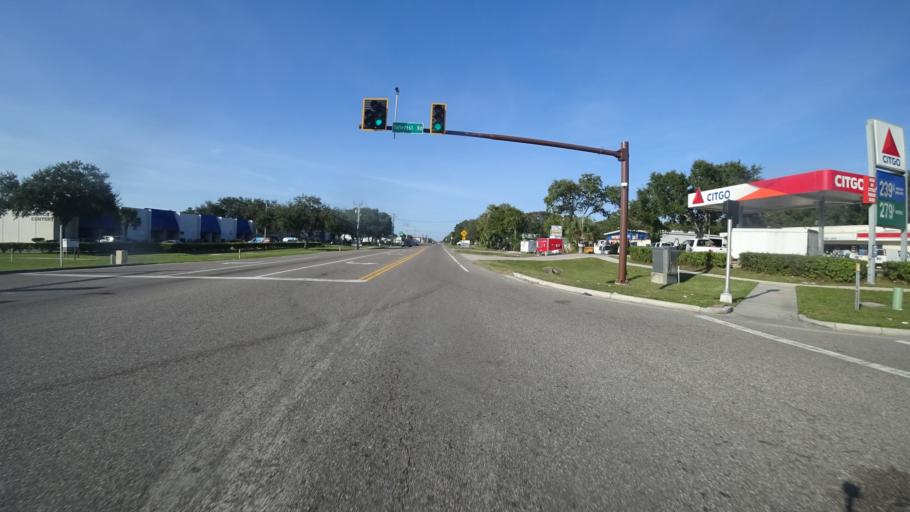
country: US
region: Florida
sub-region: Manatee County
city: Whitfield
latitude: 27.4035
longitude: -82.5468
